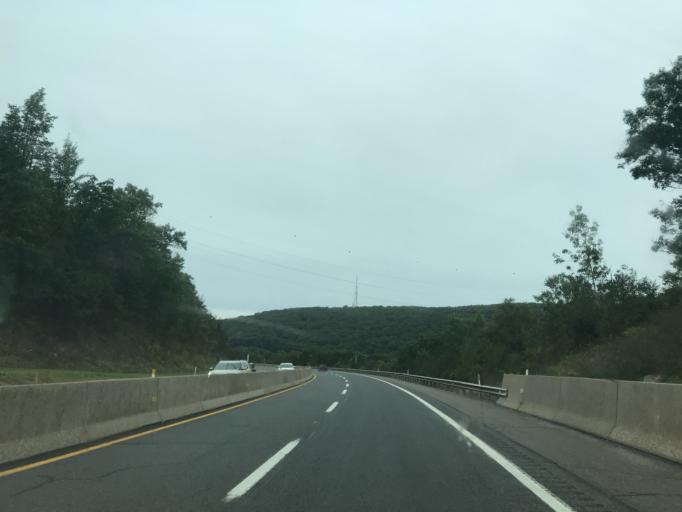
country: US
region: Pennsylvania
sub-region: Lackawanna County
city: Chinchilla
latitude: 41.4552
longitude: -75.6847
